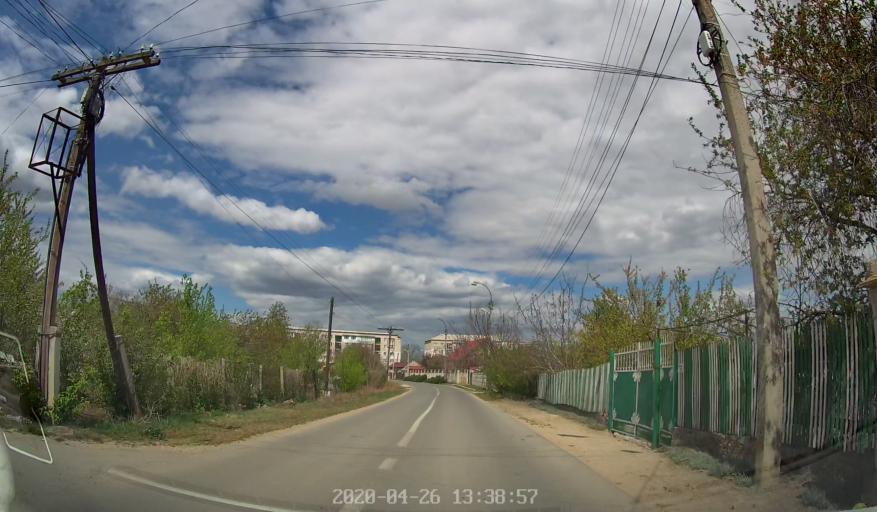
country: MD
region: Criuleni
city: Criuleni
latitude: 47.2114
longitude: 29.1650
